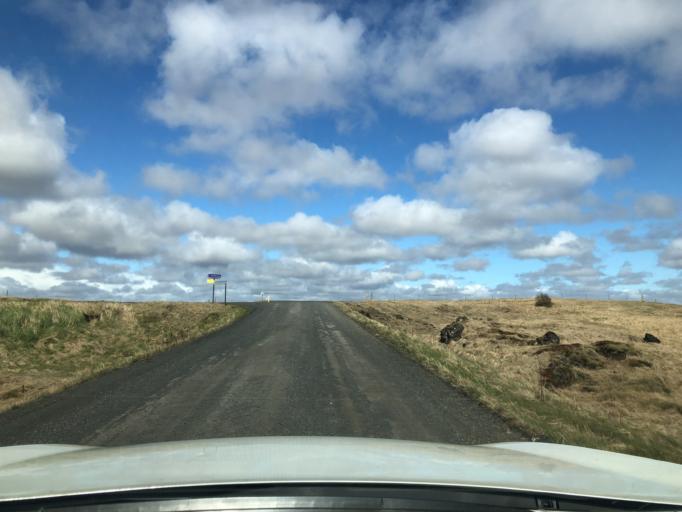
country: IS
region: South
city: Selfoss
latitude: 63.9259
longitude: -20.6765
